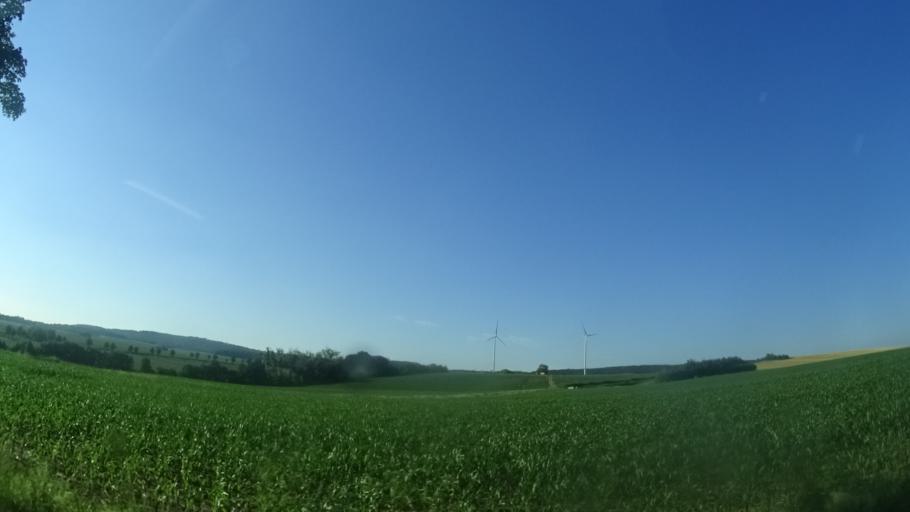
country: DE
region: Lower Saxony
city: Bad Salzdetfurth
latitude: 52.1022
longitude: 10.0480
